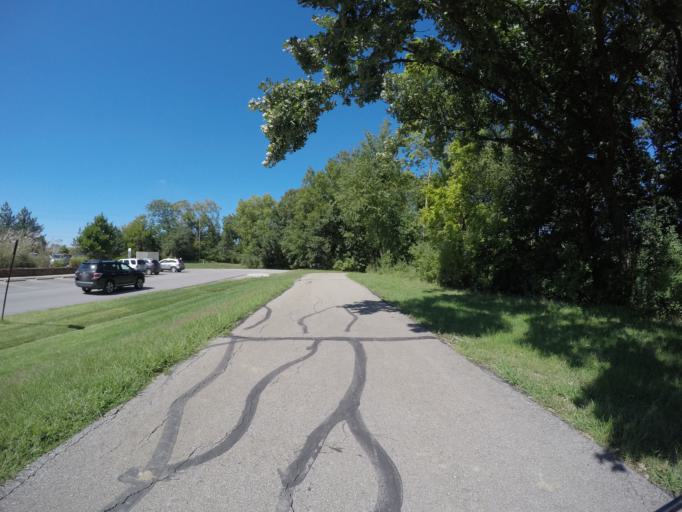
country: US
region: Kansas
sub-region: Johnson County
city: Overland Park
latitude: 38.9407
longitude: -94.6621
